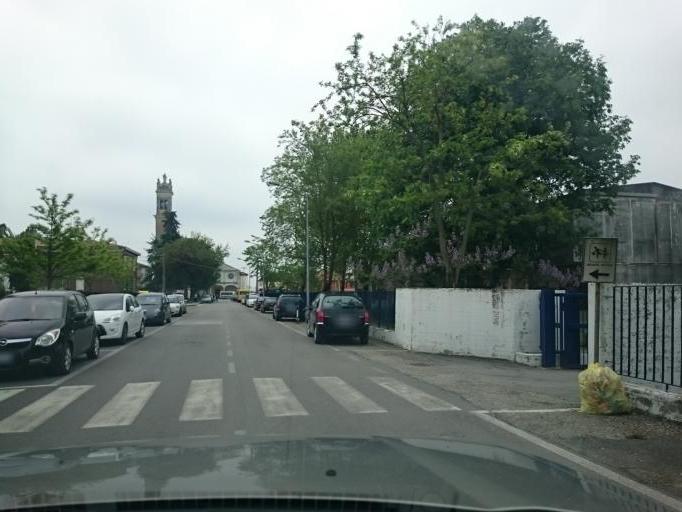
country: IT
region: Veneto
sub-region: Provincia di Padova
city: Correzzola
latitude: 45.2366
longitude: 12.0663
